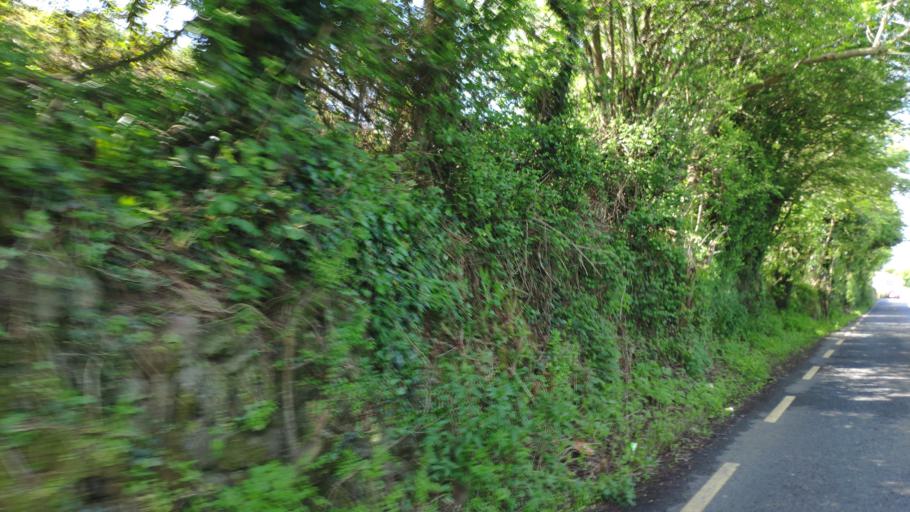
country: IE
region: Munster
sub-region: County Cork
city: Cork
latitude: 51.9224
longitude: -8.4974
